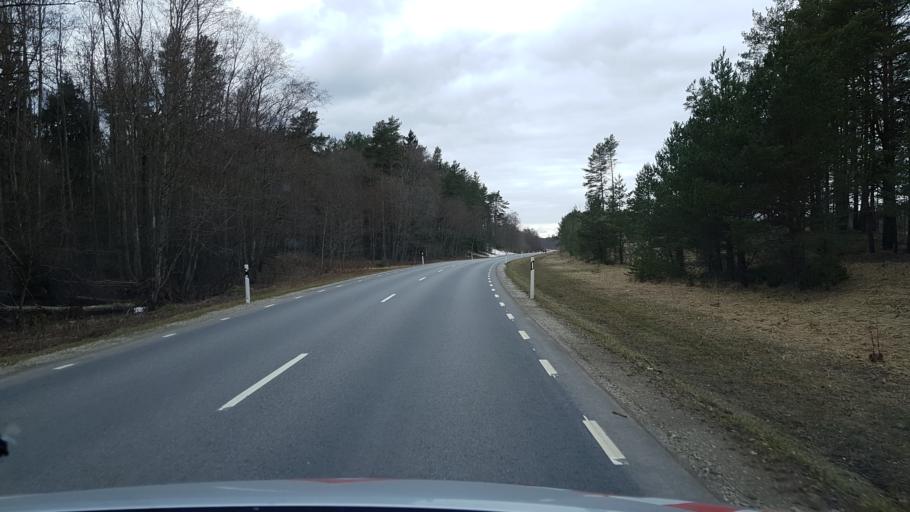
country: EE
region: Ida-Virumaa
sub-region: Narva-Joesuu linn
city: Narva-Joesuu
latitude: 59.4139
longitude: 28.0866
